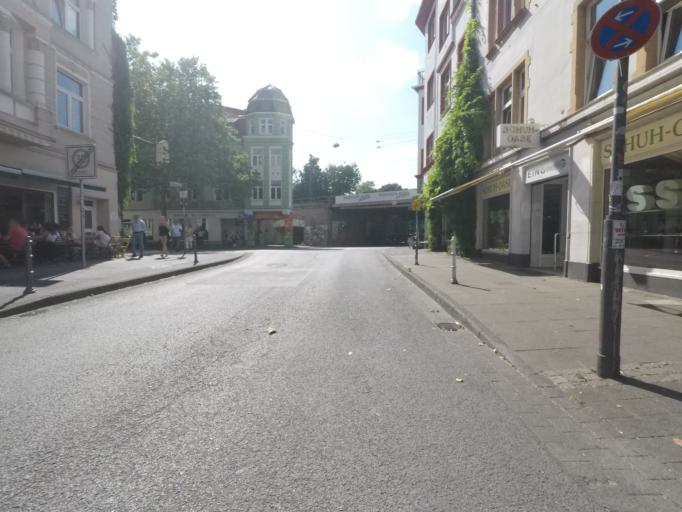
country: DE
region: North Rhine-Westphalia
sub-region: Regierungsbezirk Detmold
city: Bielefeld
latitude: 52.0253
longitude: 8.5292
